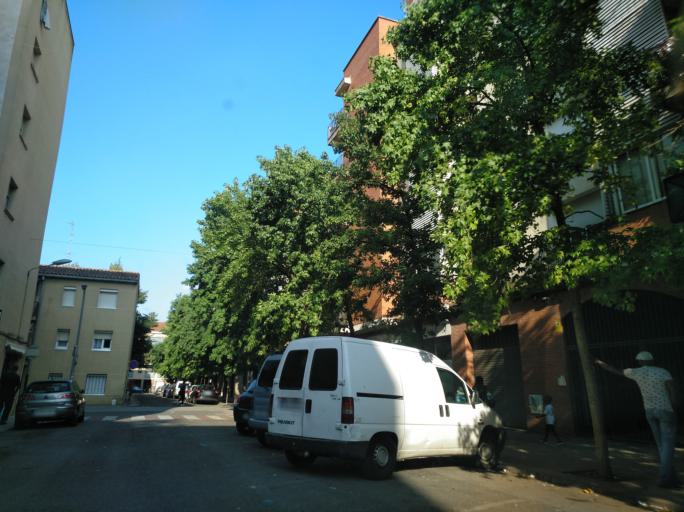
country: ES
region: Catalonia
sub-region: Provincia de Girona
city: Salt
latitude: 41.9736
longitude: 2.7923
